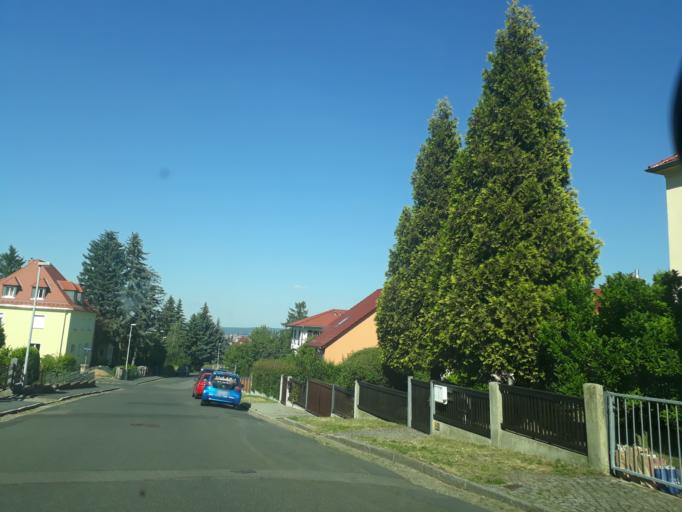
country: DE
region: Saxony
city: Bannewitz
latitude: 51.0277
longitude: 13.6911
